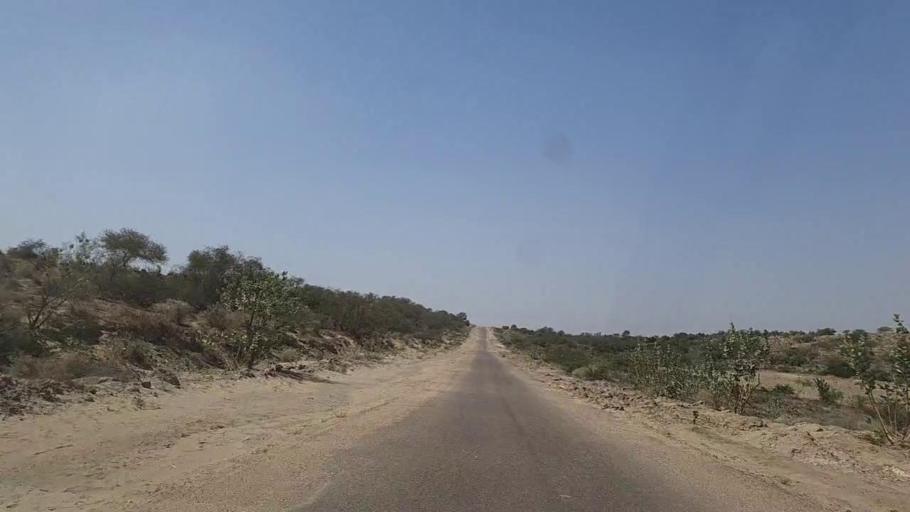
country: PK
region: Sindh
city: Diplo
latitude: 24.5516
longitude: 69.4309
